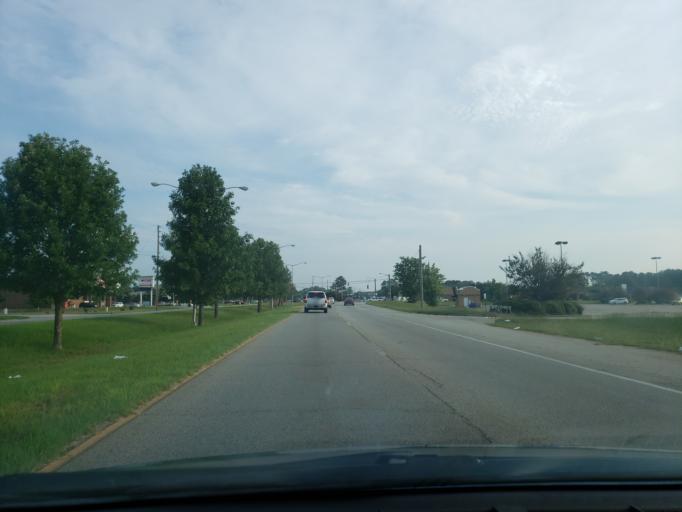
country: US
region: Georgia
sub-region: Dougherty County
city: Albany
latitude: 31.6089
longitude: -84.2227
